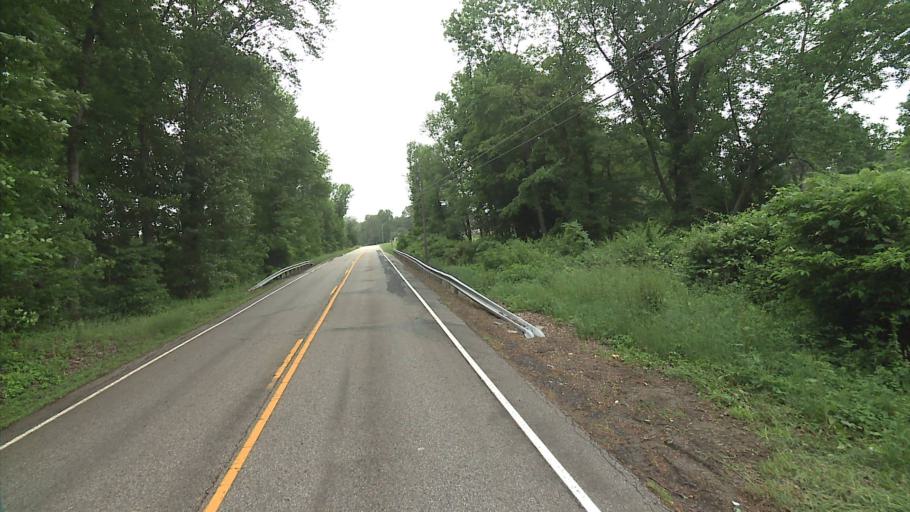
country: US
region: Connecticut
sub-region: Tolland County
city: Hebron
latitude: 41.7148
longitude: -72.3690
